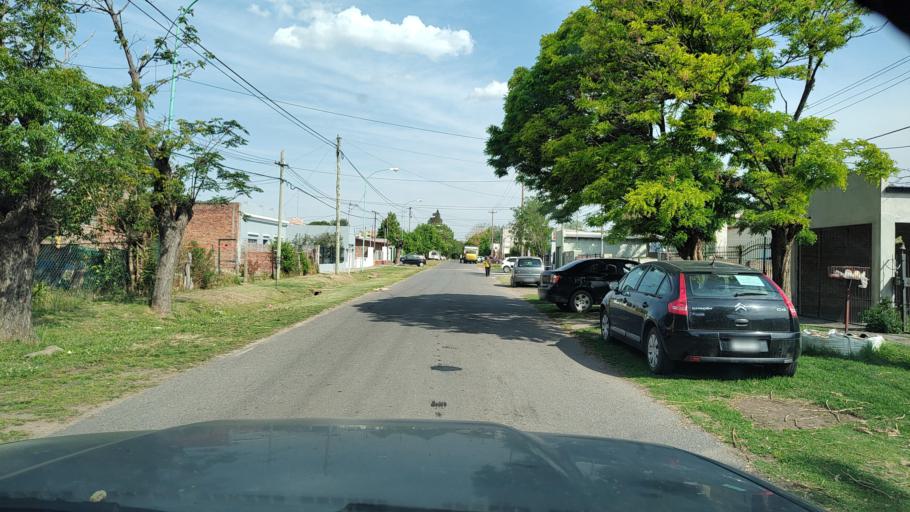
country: AR
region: Buenos Aires
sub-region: Partido de Lujan
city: Lujan
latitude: -34.5978
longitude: -59.1782
